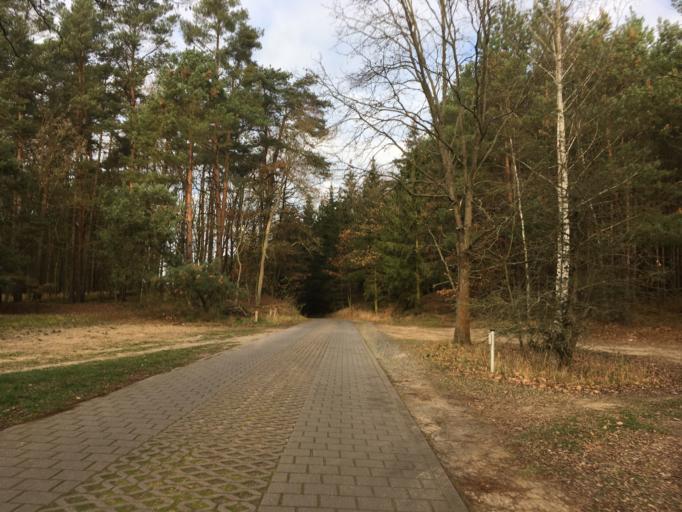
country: DE
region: Brandenburg
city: Buckow
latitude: 52.5645
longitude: 14.1258
